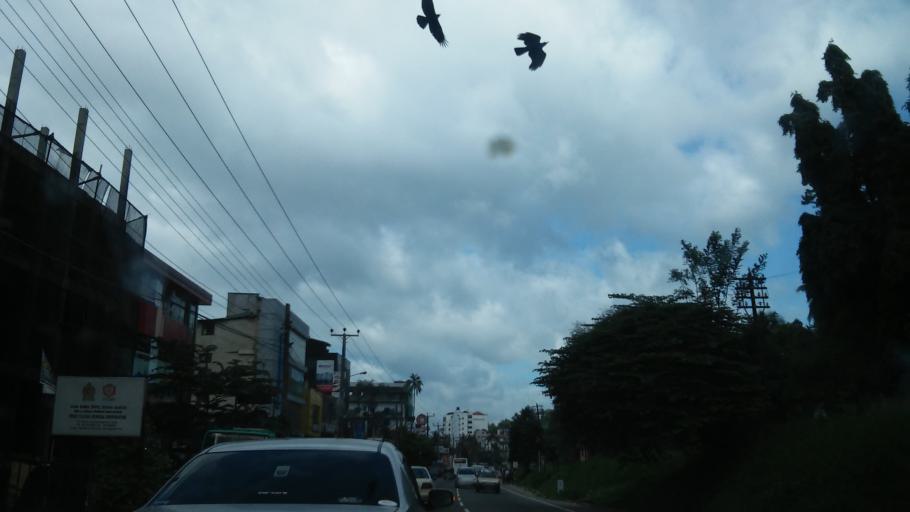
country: LK
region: Central
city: Kandy
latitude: 7.2801
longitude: 80.6209
